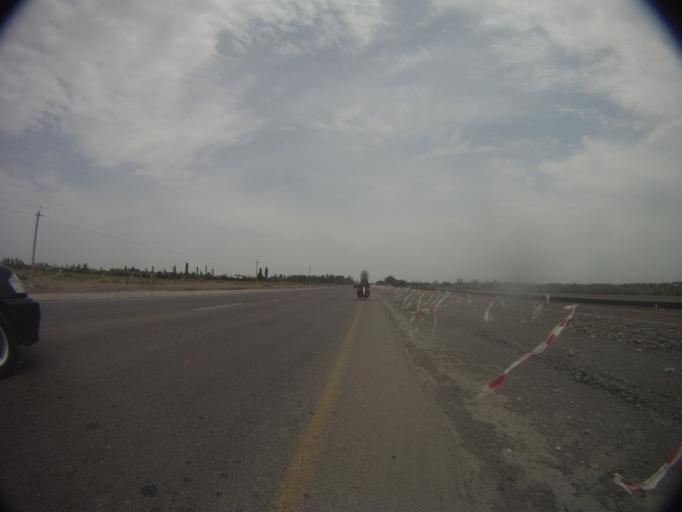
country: AZ
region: Agdas
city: Agdas
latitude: 40.5413
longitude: 47.4138
